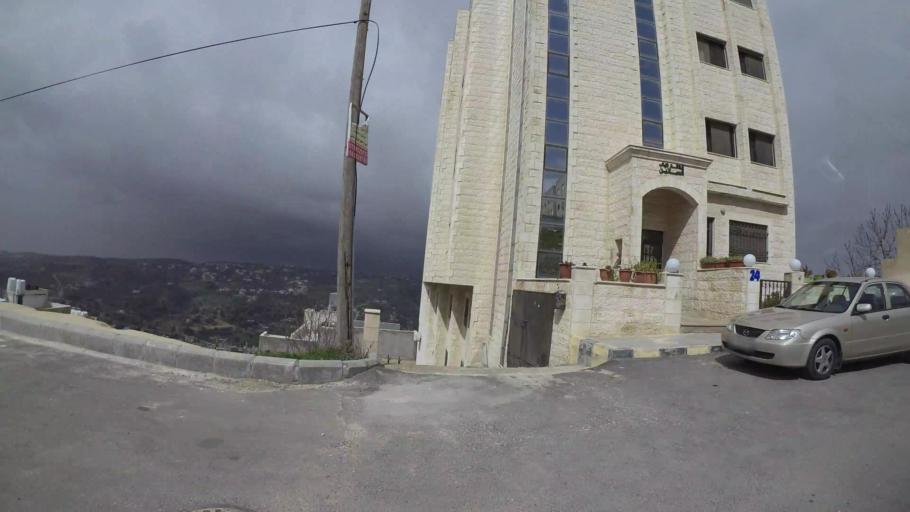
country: JO
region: Amman
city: Wadi as Sir
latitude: 31.9523
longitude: 35.8276
